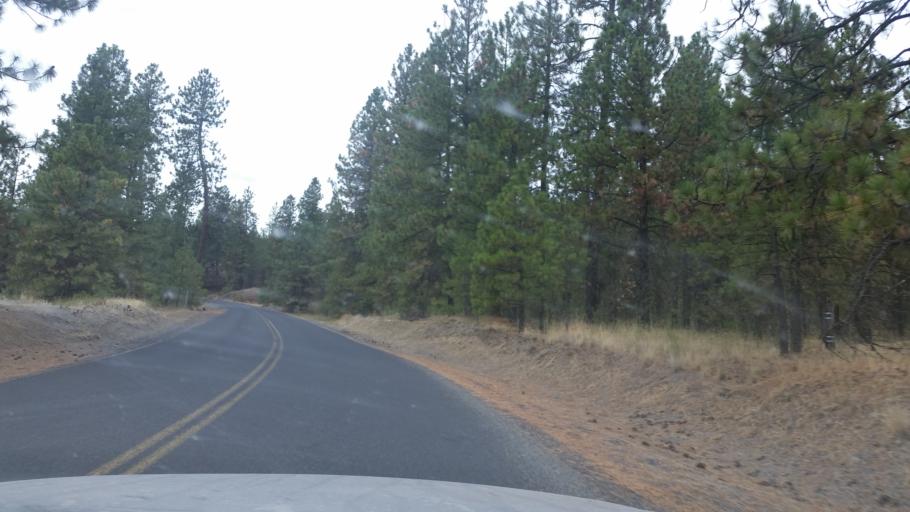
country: US
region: Washington
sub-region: Spokane County
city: Spokane
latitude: 47.6555
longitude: -117.4801
